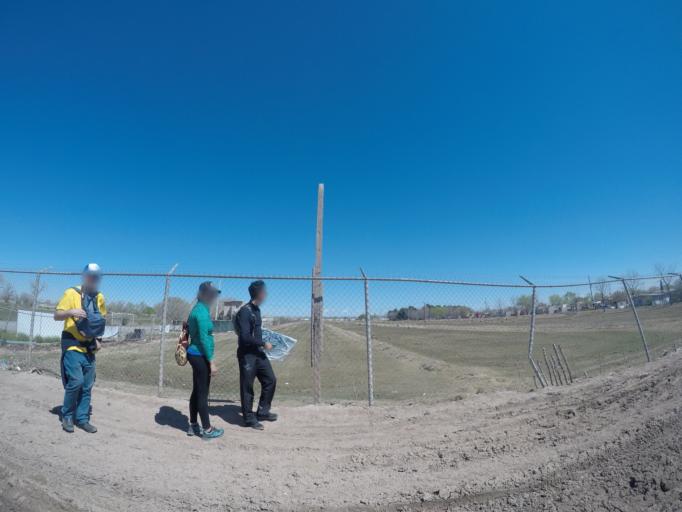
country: US
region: Texas
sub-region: El Paso County
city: Socorro Mission Number 1 Colonia
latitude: 31.6089
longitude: -106.3129
